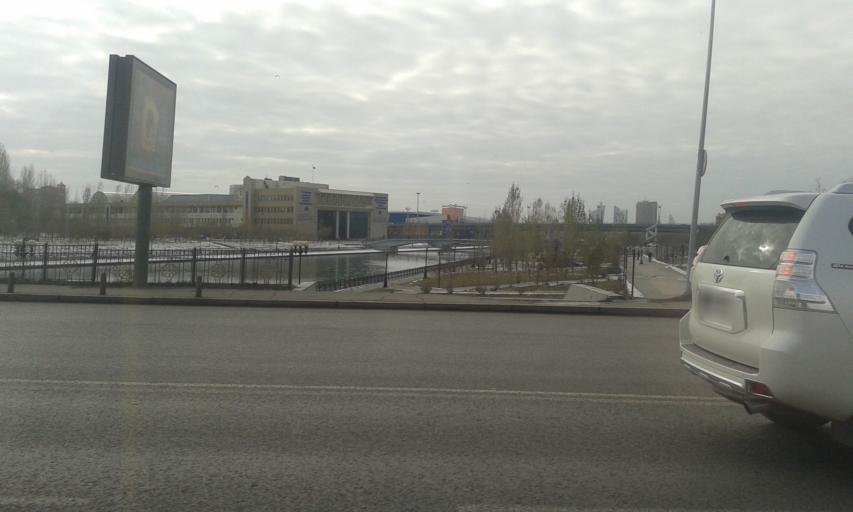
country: KZ
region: Astana Qalasy
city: Astana
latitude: 51.1608
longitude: 71.4692
